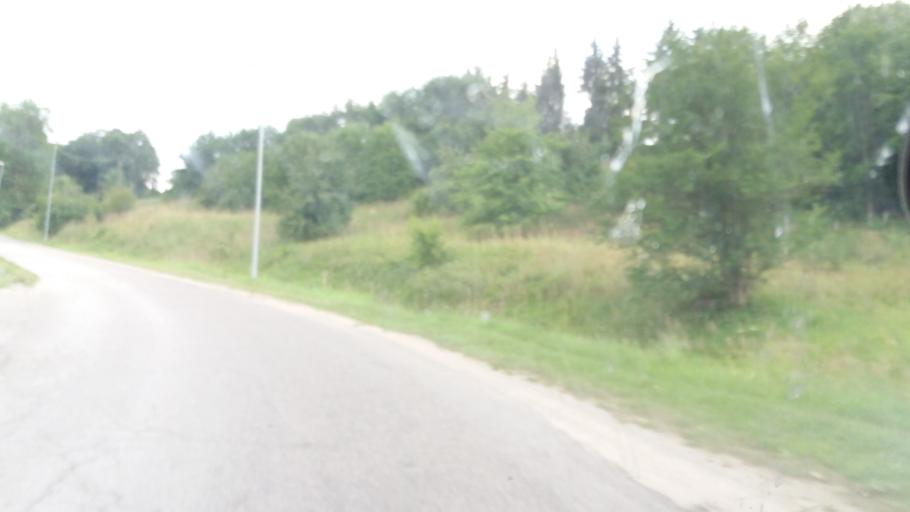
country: LV
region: Talsu Rajons
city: Sabile
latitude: 57.0409
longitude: 22.5682
